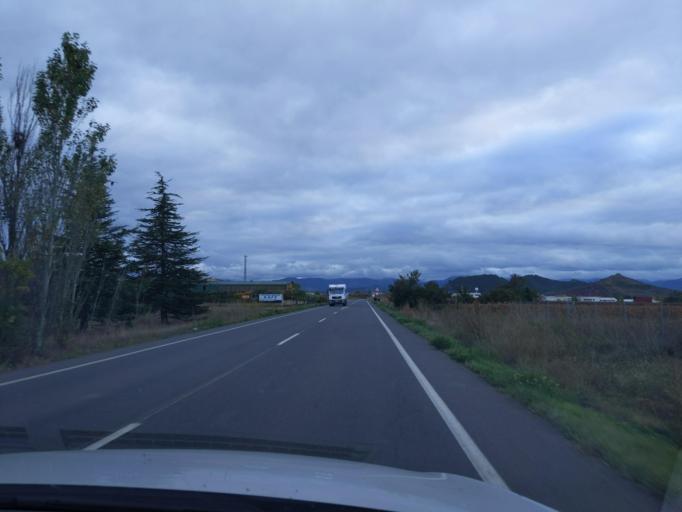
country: ES
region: La Rioja
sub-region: Provincia de La Rioja
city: Urunuela
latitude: 42.4319
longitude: -2.7159
